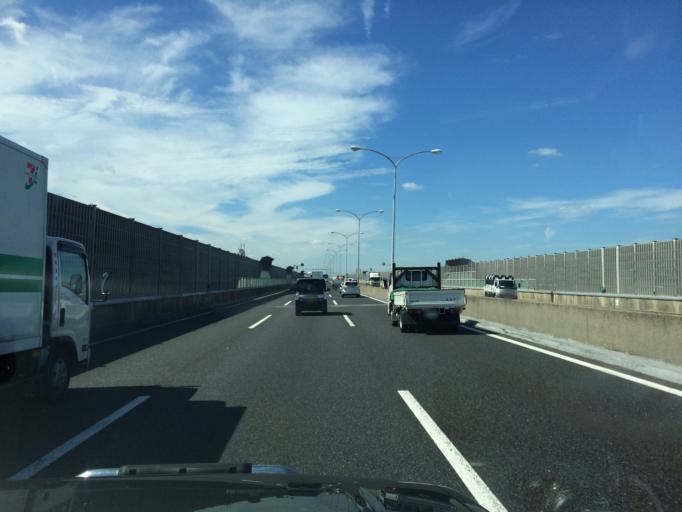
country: JP
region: Osaka
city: Matsubara
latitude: 34.5377
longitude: 135.5417
